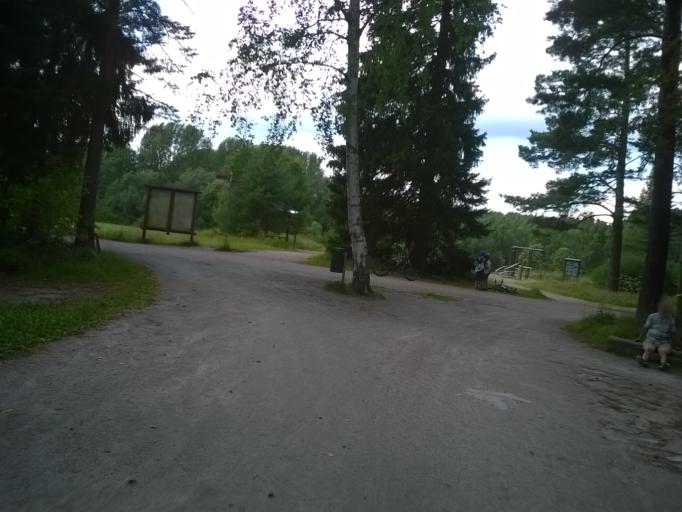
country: FI
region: Uusimaa
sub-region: Helsinki
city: Teekkarikylae
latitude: 60.2671
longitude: 24.9011
